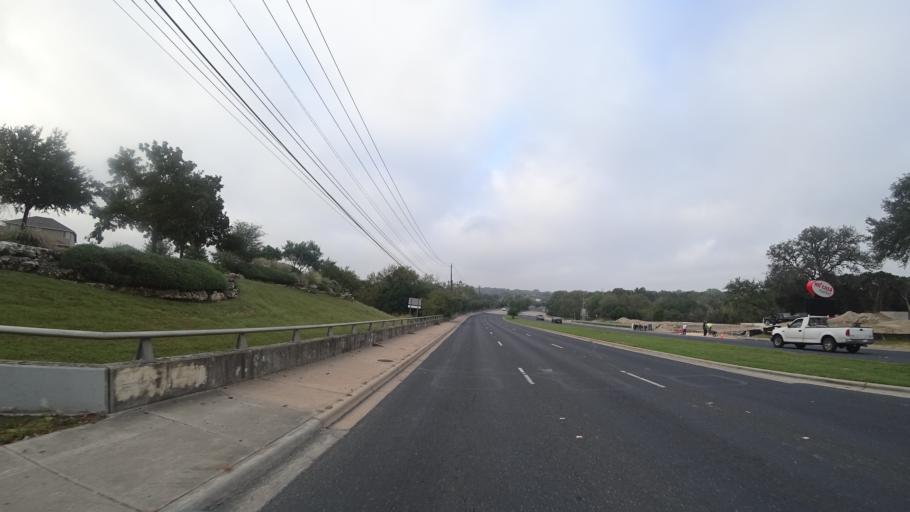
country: US
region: Texas
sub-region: Travis County
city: Wells Branch
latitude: 30.3766
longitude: -97.6590
